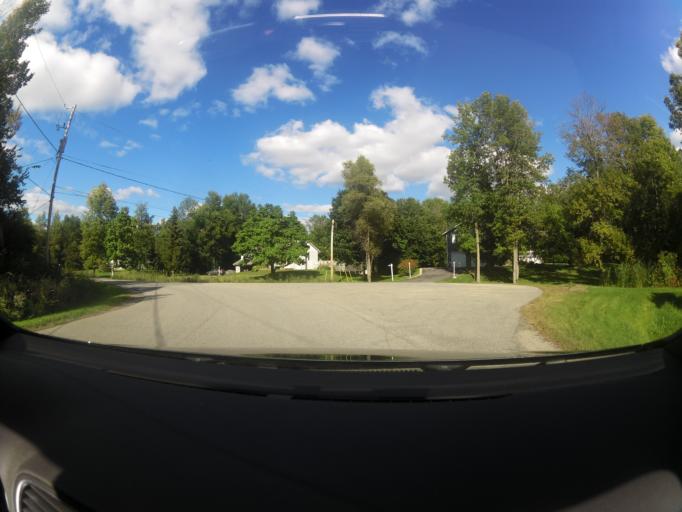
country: CA
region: Ontario
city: Carleton Place
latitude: 45.1385
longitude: -76.0728
